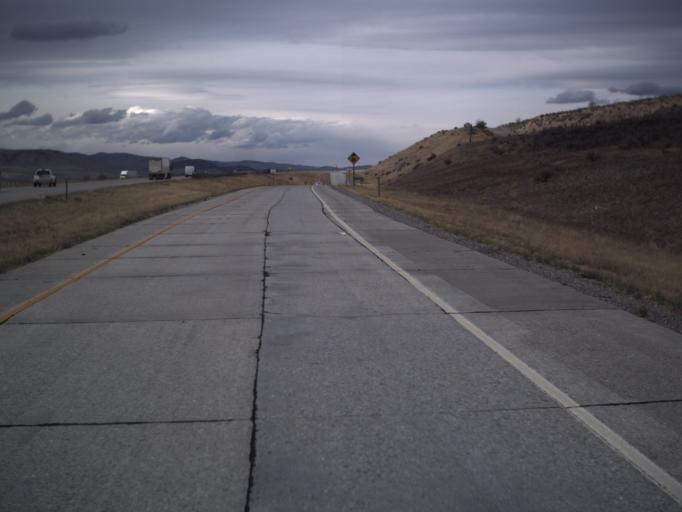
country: US
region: Idaho
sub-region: Oneida County
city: Malad City
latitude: 41.9733
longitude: -112.1864
